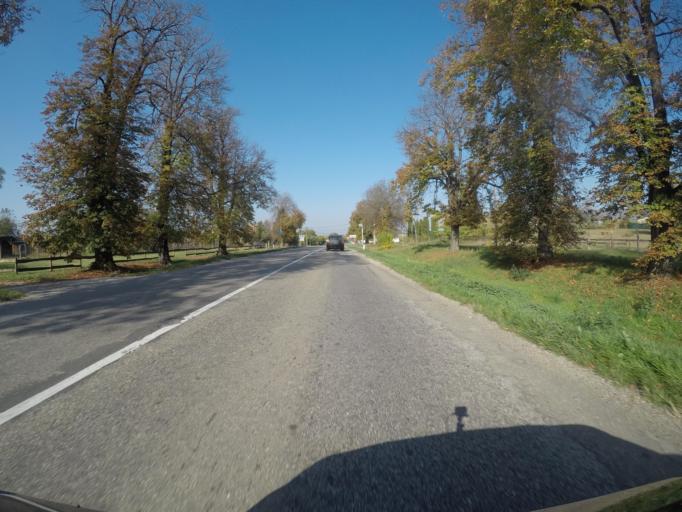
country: HU
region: Tolna
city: Szedres
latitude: 46.4691
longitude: 18.6865
